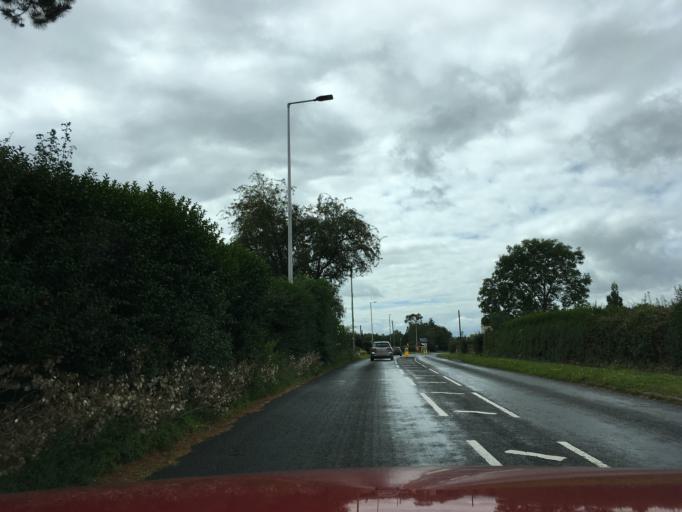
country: GB
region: England
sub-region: Devon
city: Cullompton
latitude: 50.8830
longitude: -3.3765
